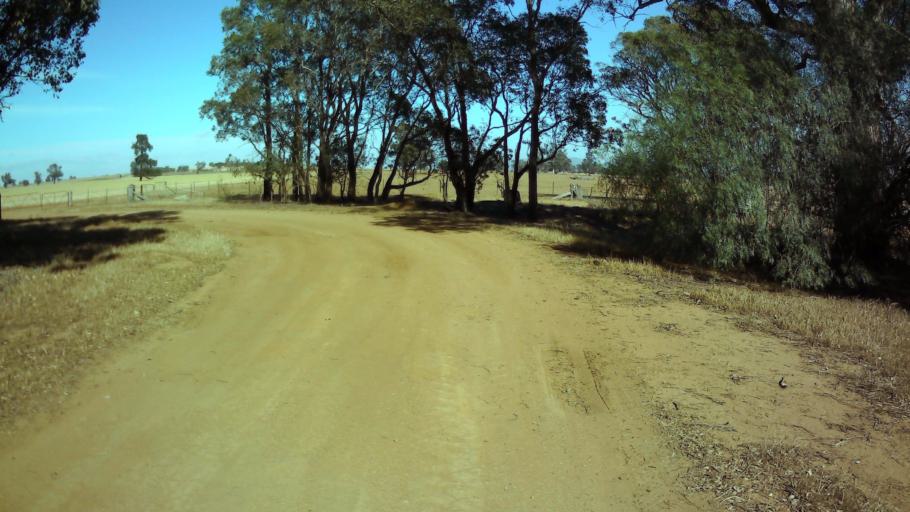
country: AU
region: New South Wales
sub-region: Weddin
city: Grenfell
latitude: -34.0462
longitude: 148.2704
